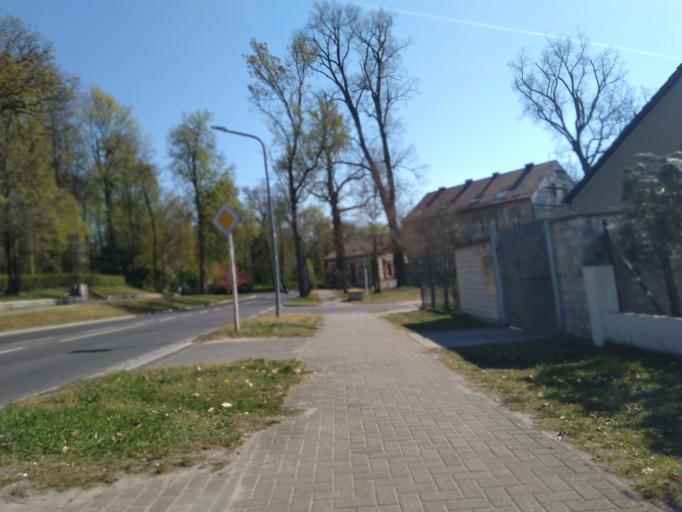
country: DE
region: Brandenburg
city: Biesenthal
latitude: 52.7644
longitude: 13.6454
